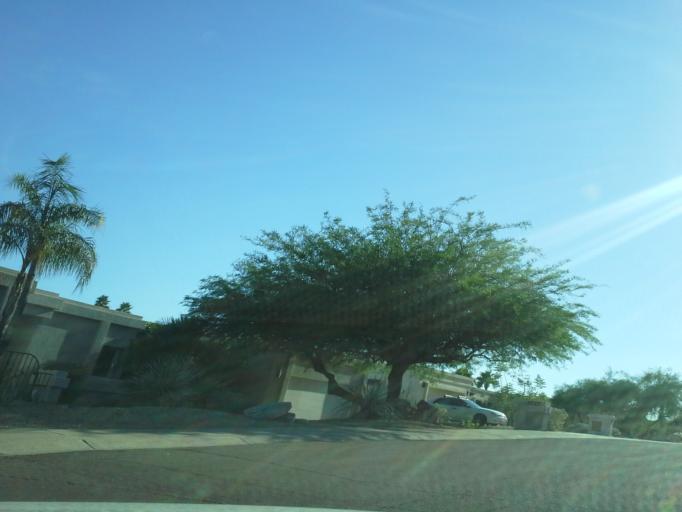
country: US
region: Arizona
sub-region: Maricopa County
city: Paradise Valley
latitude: 33.5614
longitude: -112.0444
